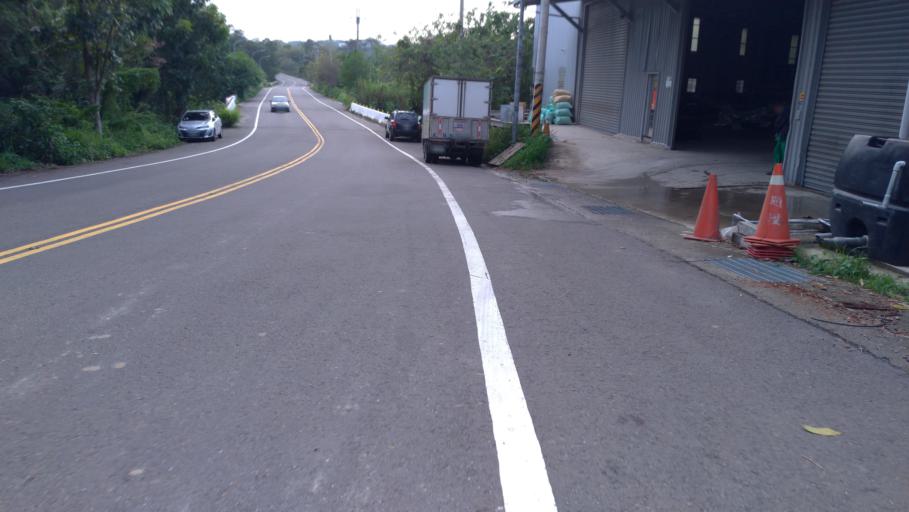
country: TW
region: Taiwan
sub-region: Hsinchu
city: Hsinchu
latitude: 24.7605
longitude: 120.9876
